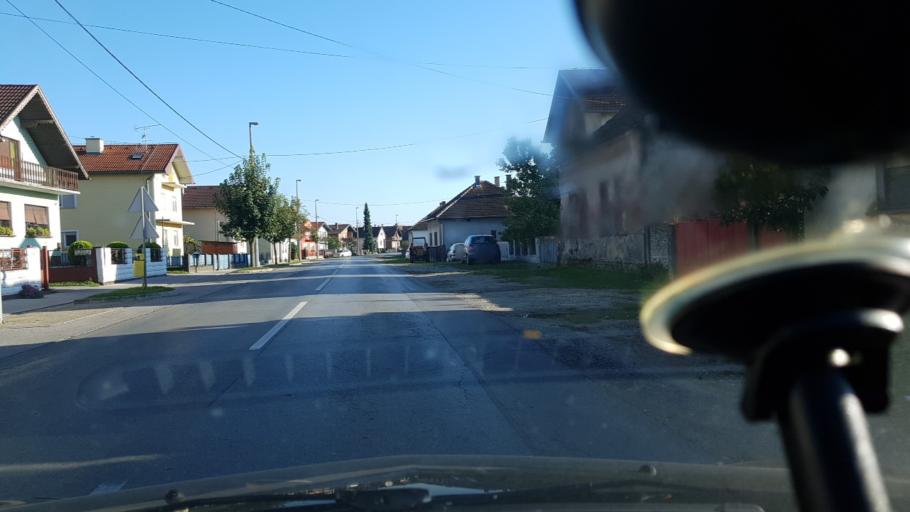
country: HR
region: Koprivnicko-Krizevacka
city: Kalinovac
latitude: 46.0446
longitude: 17.0570
